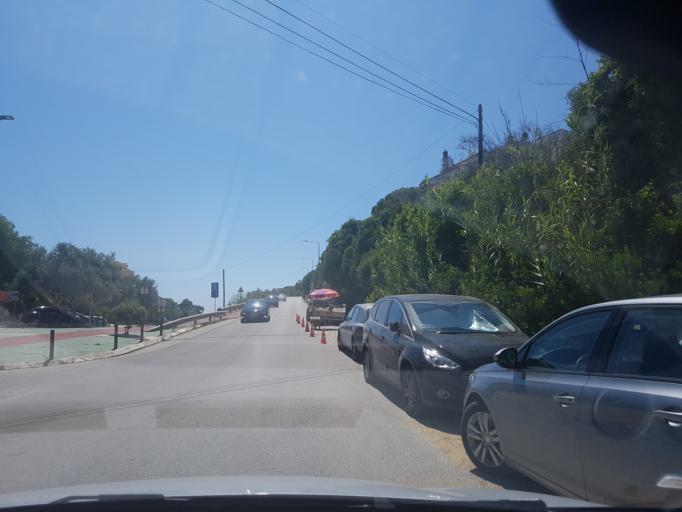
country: PT
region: Faro
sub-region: Lagoa
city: Carvoeiro
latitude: 37.0928
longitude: -8.4516
